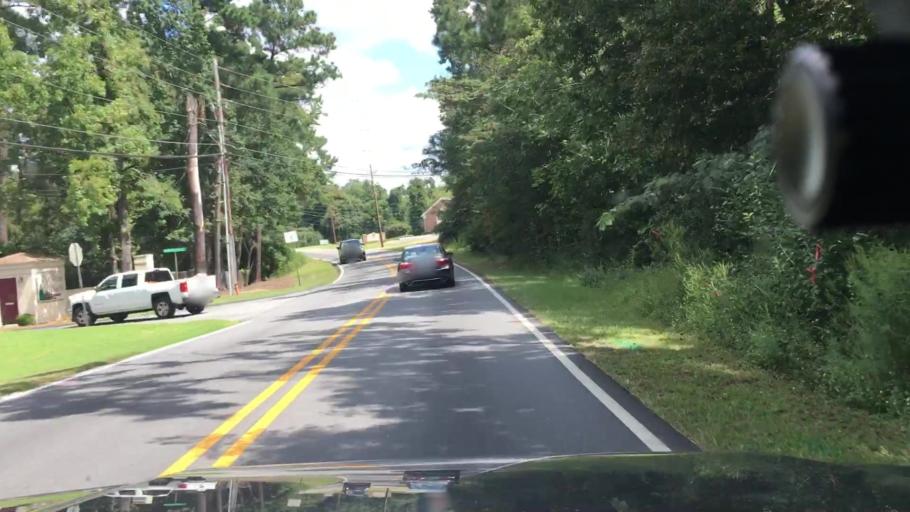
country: US
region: Georgia
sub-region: Bibb County
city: Macon
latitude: 32.8732
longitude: -83.6896
